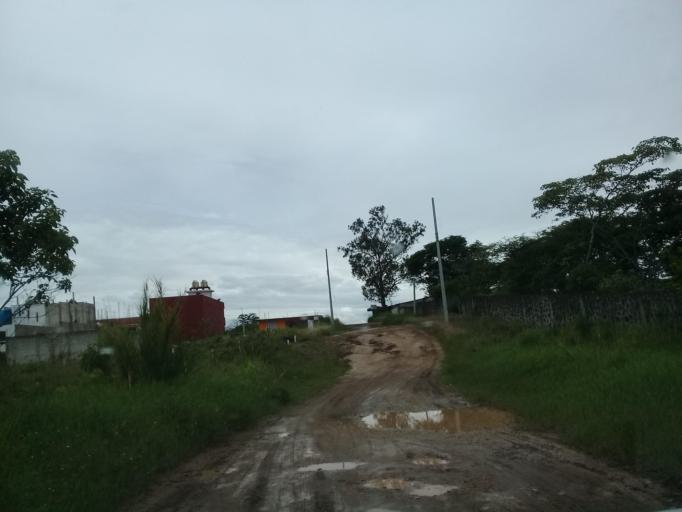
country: MX
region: Veracruz
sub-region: Emiliano Zapata
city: Jacarandas
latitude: 19.4957
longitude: -96.8430
